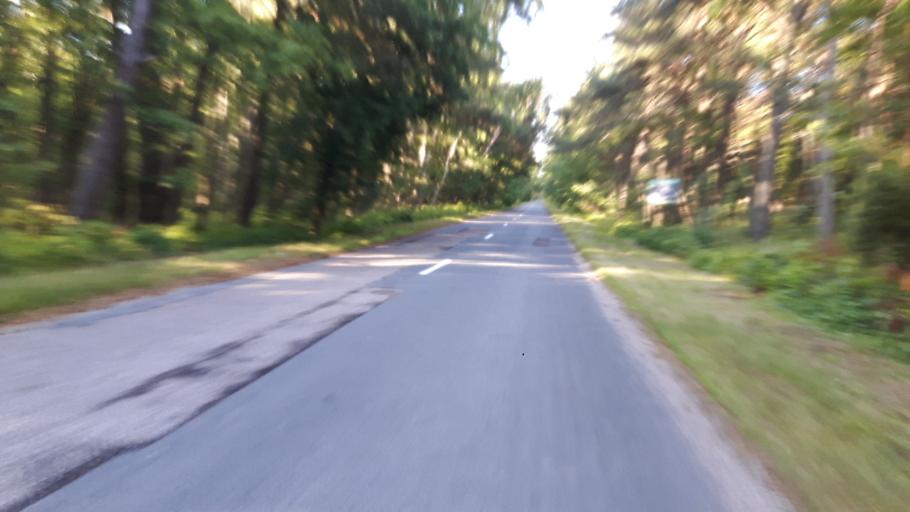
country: LT
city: Nida
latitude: 55.2412
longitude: 20.9151
